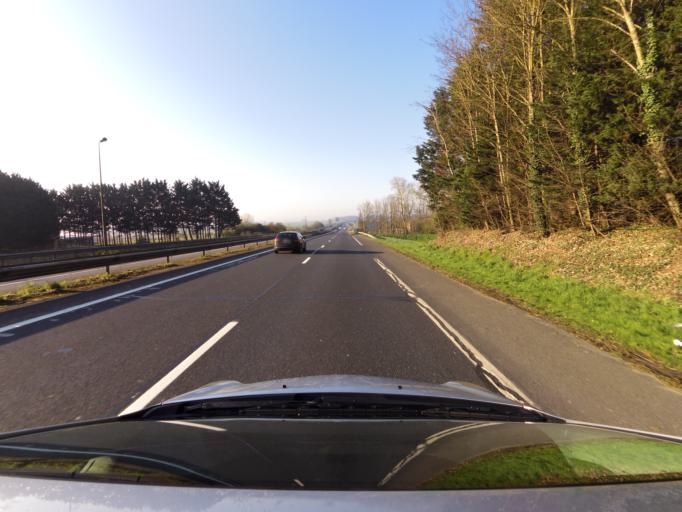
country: FR
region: Lower Normandy
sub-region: Departement du Calvados
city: Saint-Germain-la-Blanche-Herbe
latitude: 49.1859
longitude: -0.4250
